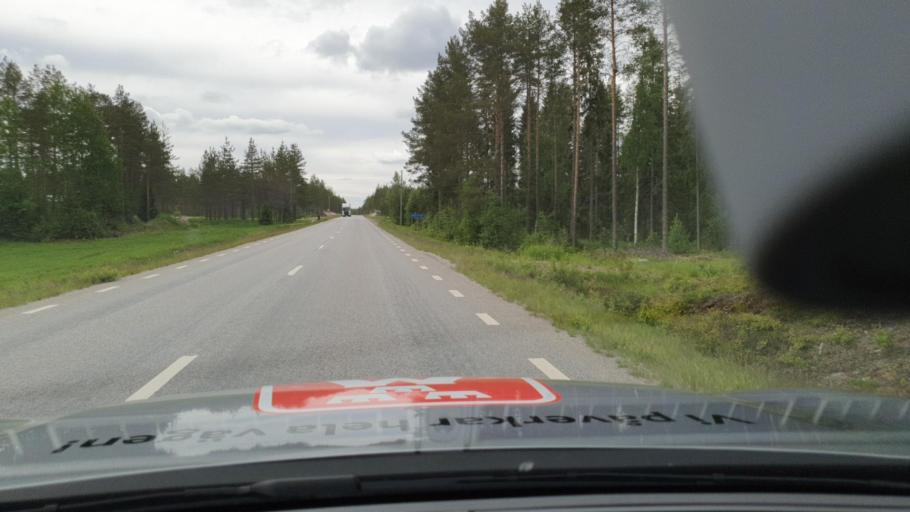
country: SE
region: Norrbotten
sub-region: Kalix Kommun
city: Kalix
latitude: 65.9663
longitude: 23.4578
